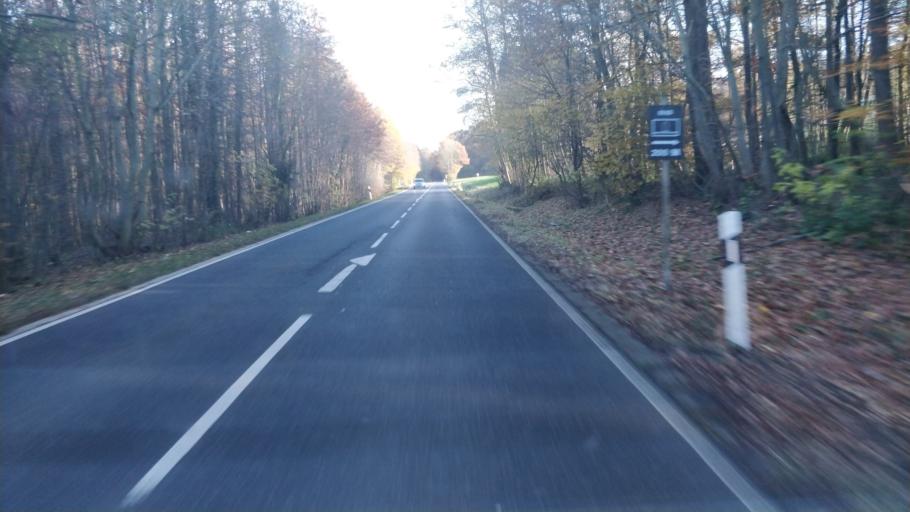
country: DE
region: North Rhine-Westphalia
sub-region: Regierungsbezirk Koln
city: Rheinbach
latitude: 50.6167
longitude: 6.9037
